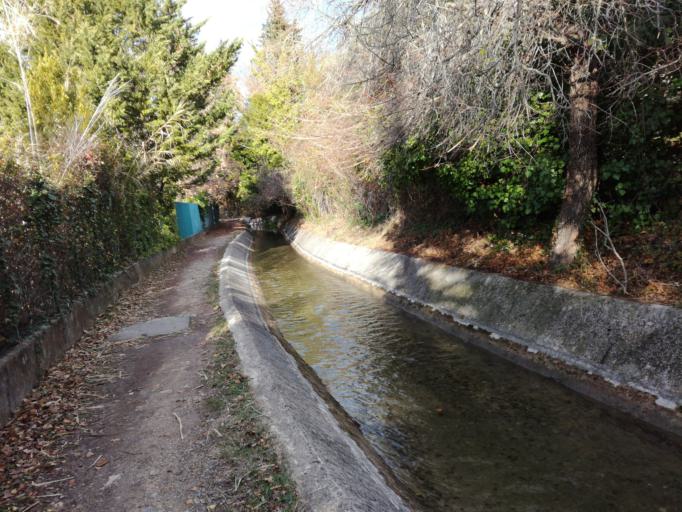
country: FR
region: Provence-Alpes-Cote d'Azur
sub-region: Departement des Alpes-Maritimes
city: Mouans-Sartoux
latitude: 43.6231
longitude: 6.9810
